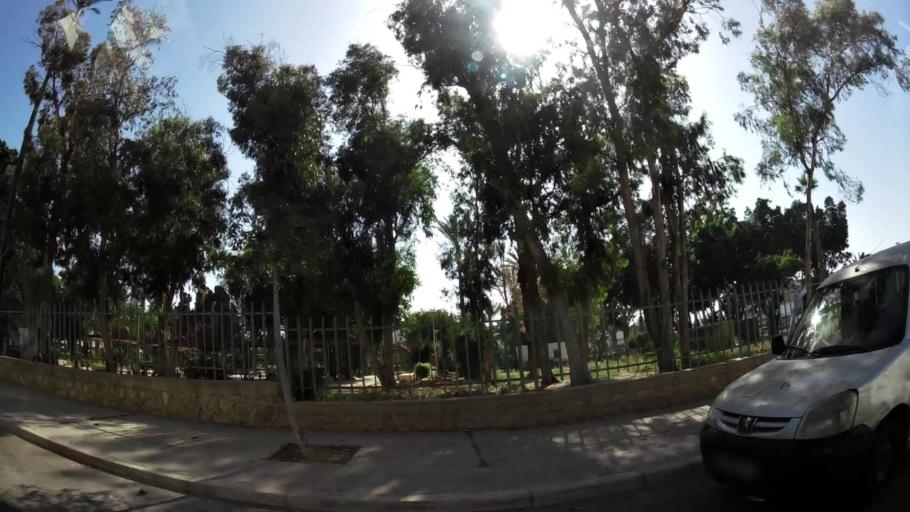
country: MA
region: Souss-Massa-Draa
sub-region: Agadir-Ida-ou-Tnan
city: Agadir
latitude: 30.4134
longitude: -9.5862
